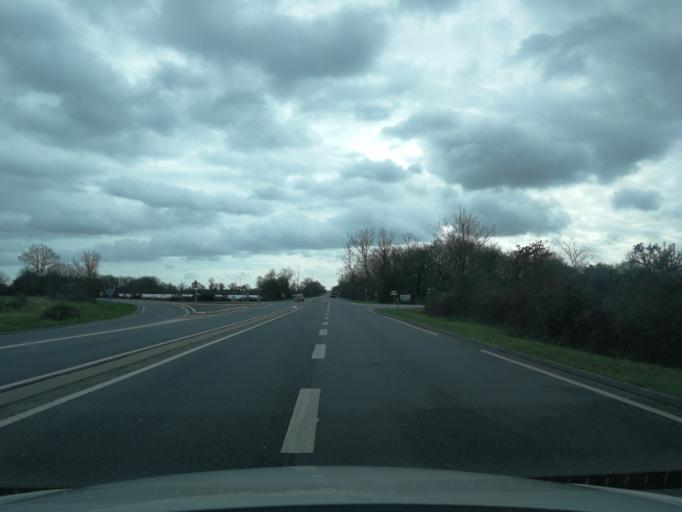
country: FR
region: Pays de la Loire
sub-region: Departement de la Loire-Atlantique
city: Geneston
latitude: 47.0377
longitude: -1.5071
